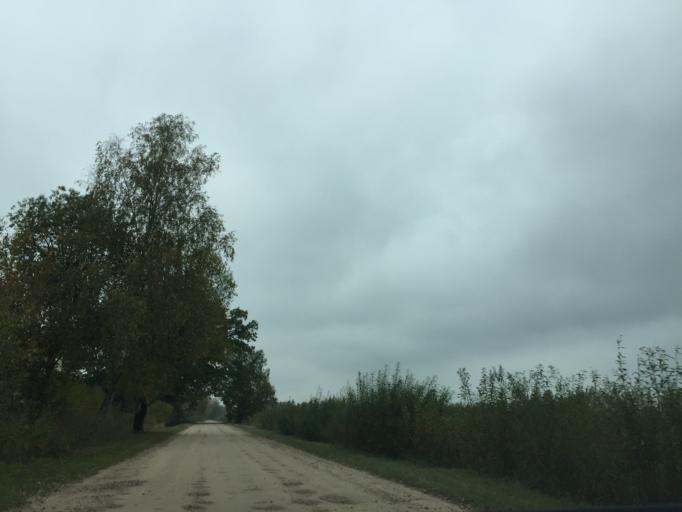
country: LV
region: Ozolnieku
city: Ozolnieki
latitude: 56.6861
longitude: 23.7485
